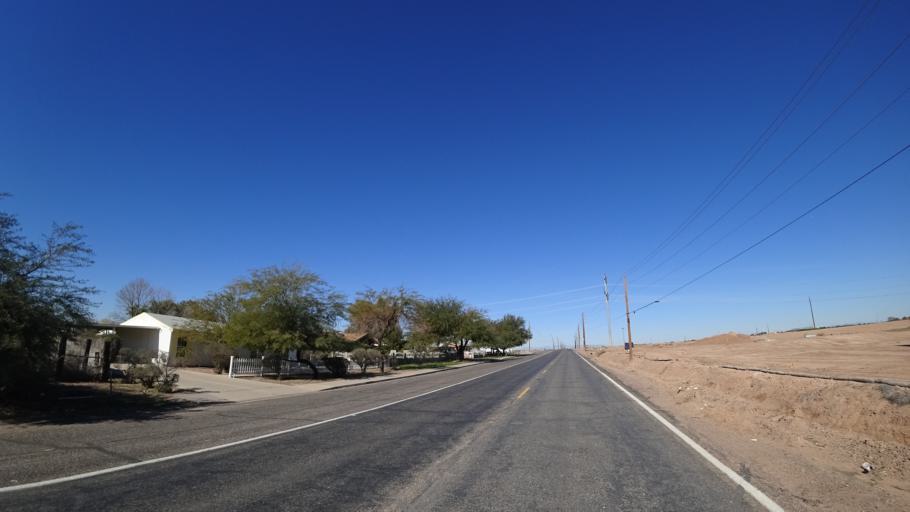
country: US
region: Arizona
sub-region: Maricopa County
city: Tolleson
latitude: 33.3976
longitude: -112.2891
